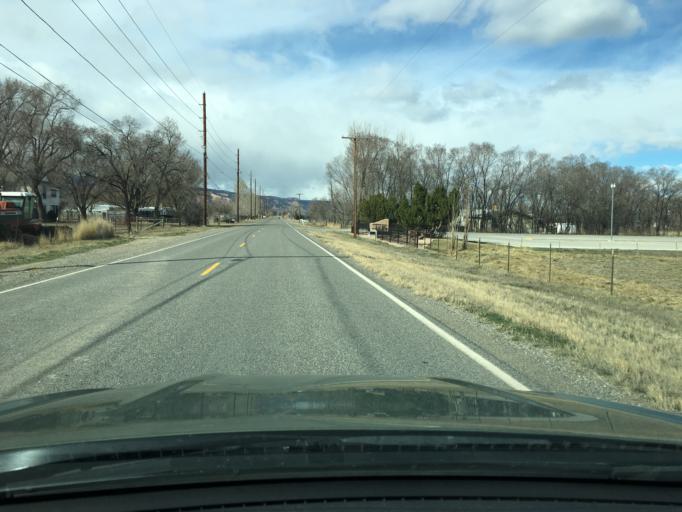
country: US
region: Colorado
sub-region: Mesa County
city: Redlands
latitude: 39.1209
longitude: -108.6200
